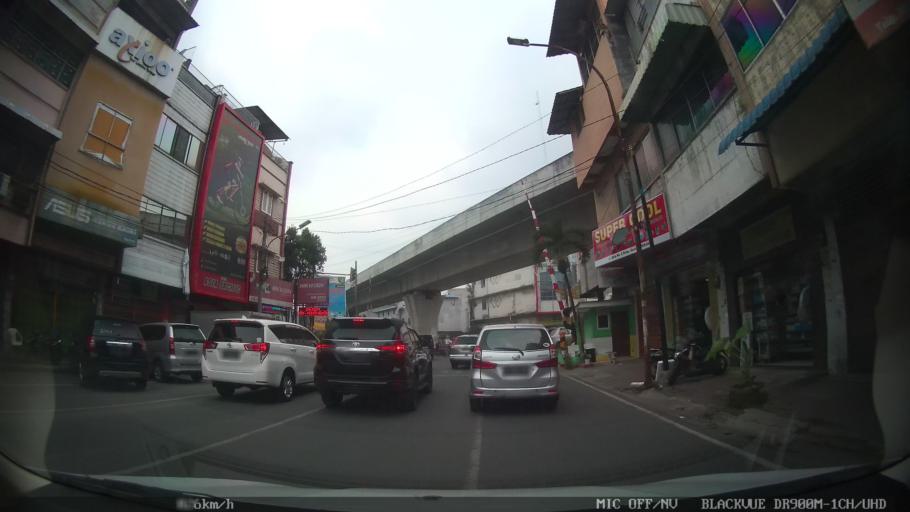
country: ID
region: North Sumatra
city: Medan
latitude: 3.5832
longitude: 98.6880
